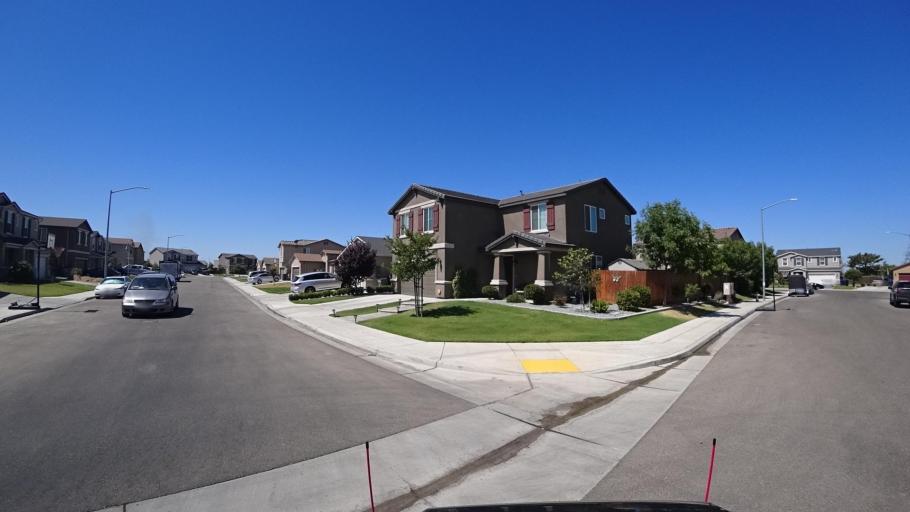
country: US
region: California
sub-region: Fresno County
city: Sunnyside
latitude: 36.7200
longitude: -119.6716
